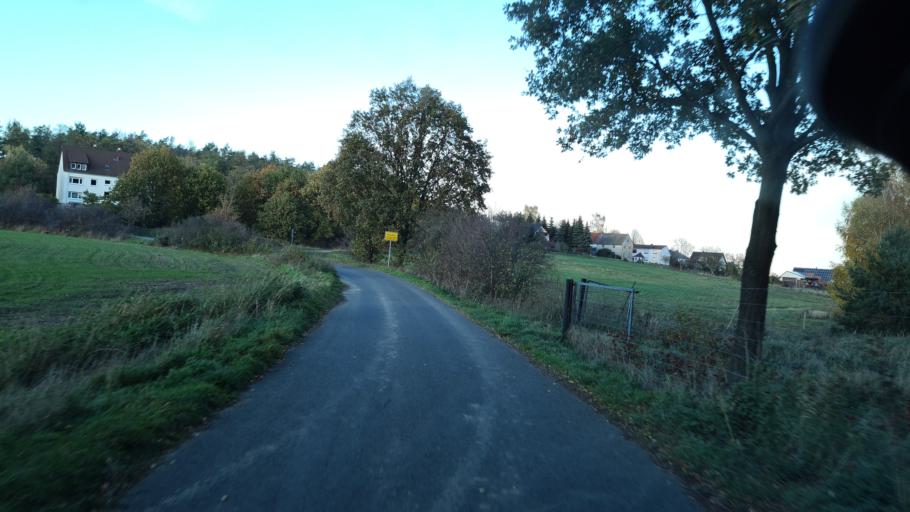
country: DE
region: Saxony
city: Belgern
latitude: 51.4440
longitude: 13.1123
